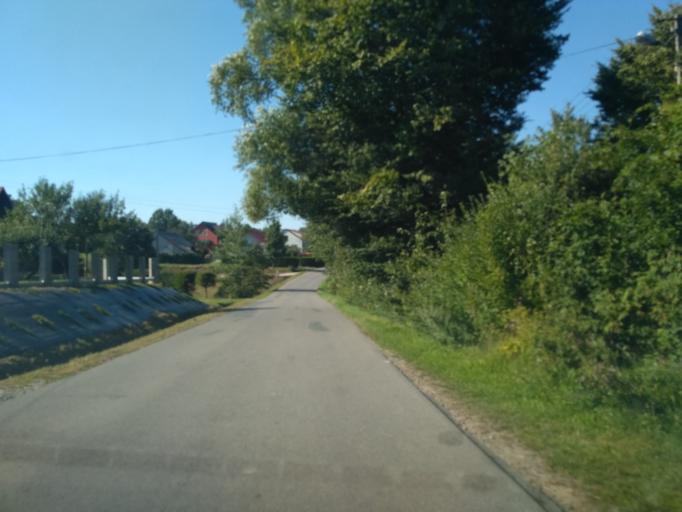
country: PL
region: Subcarpathian Voivodeship
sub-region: Powiat strzyzowski
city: Wysoka Strzyzowska
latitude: 49.8247
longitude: 21.7392
